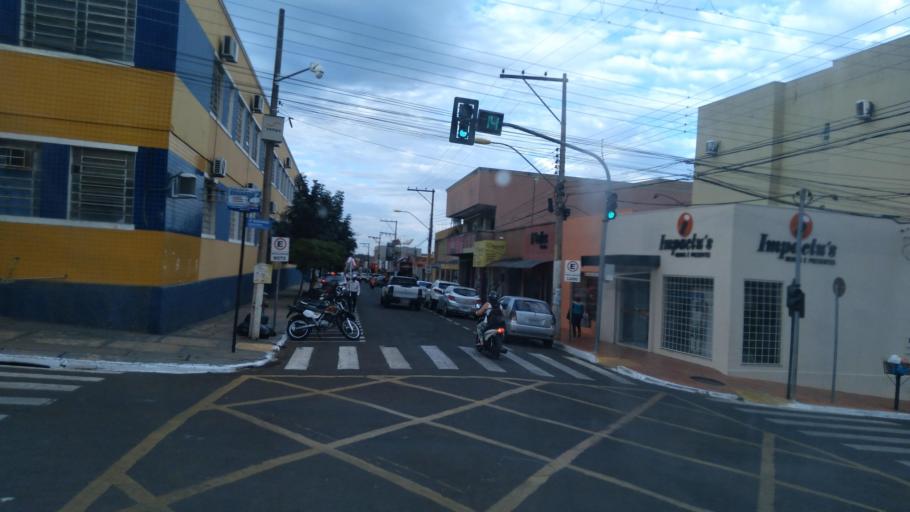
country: BR
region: Goias
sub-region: Mineiros
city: Mineiros
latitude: -17.5689
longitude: -52.5549
